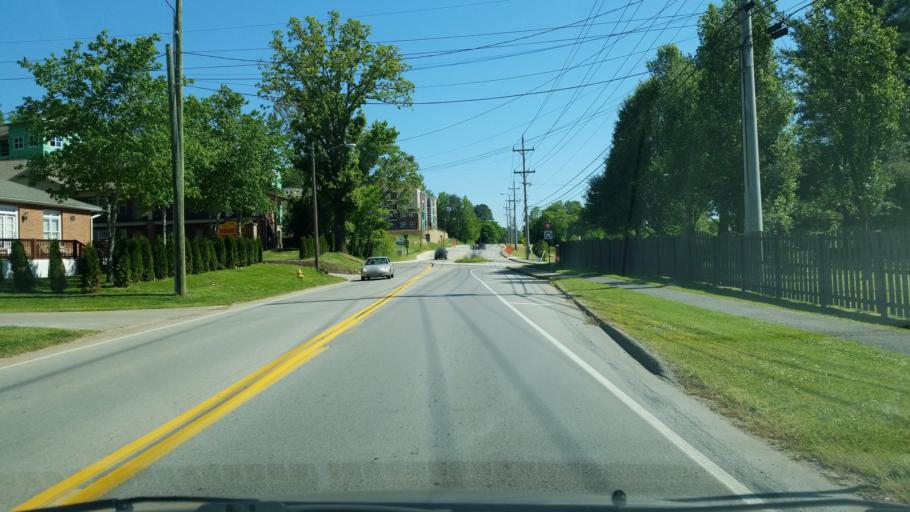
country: US
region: Tennessee
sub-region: Hamilton County
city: Signal Mountain
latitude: 35.1101
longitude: -85.3240
